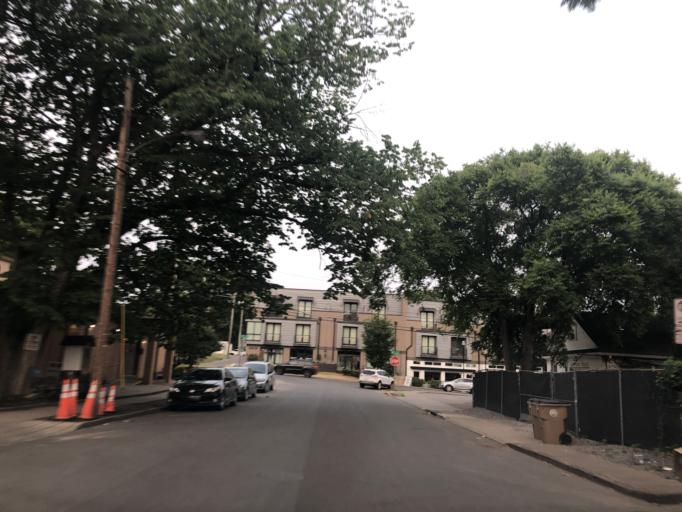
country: US
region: Tennessee
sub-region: Davidson County
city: Oak Hill
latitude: 36.1241
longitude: -86.7904
